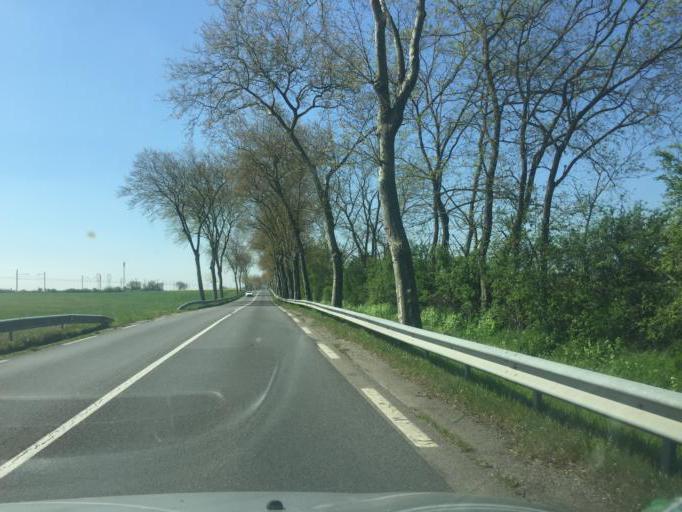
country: FR
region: Rhone-Alpes
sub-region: Departement de l'Ain
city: Perouges
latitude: 45.8804
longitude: 5.1647
